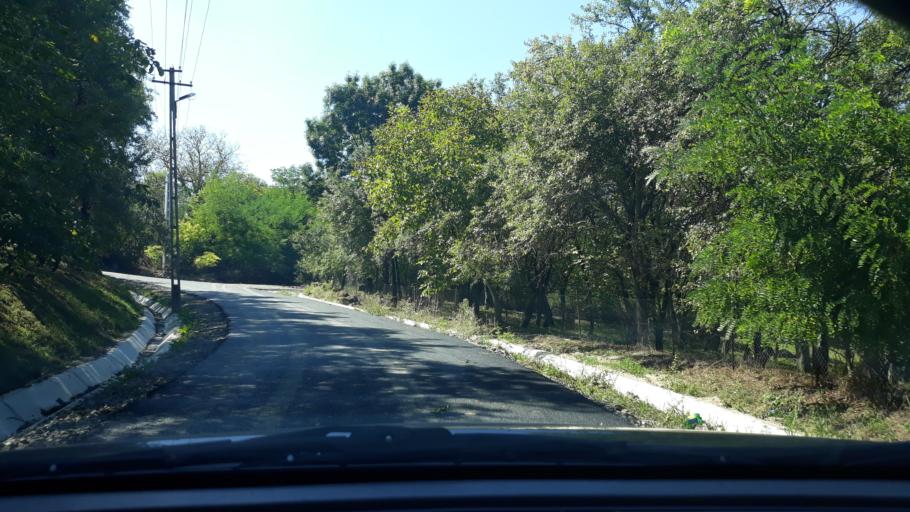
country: RO
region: Salaj
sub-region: Comuna Dobrin
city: Dobrin
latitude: 47.2951
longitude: 23.0870
